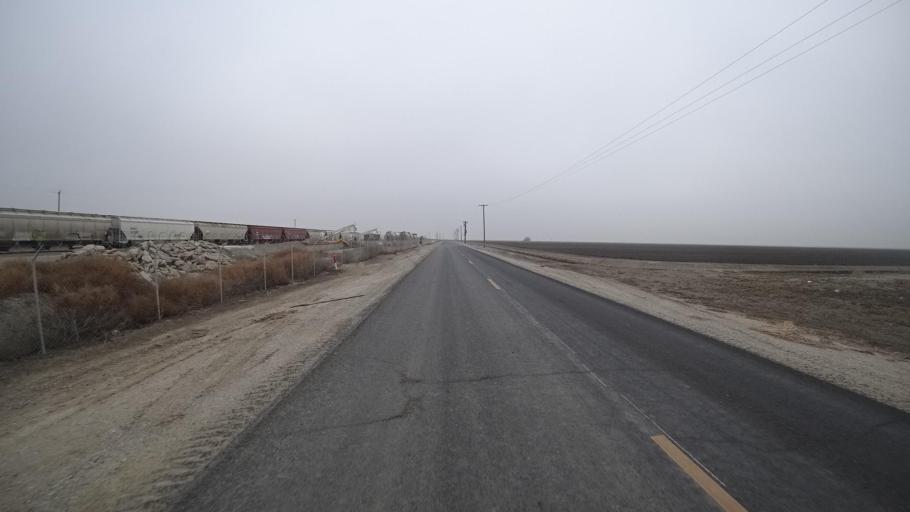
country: US
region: California
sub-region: Kern County
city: Rosedale
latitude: 35.1804
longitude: -119.1936
